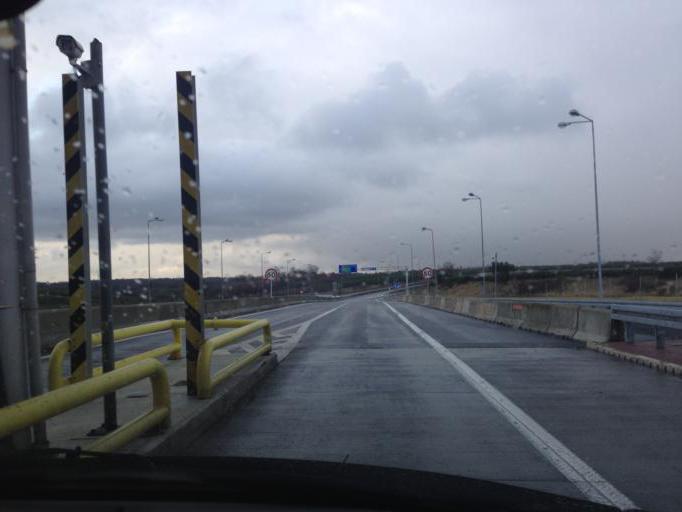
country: PL
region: Opole Voivodeship
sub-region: Powiat strzelecki
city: Ujazd
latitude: 50.4488
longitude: 18.3474
